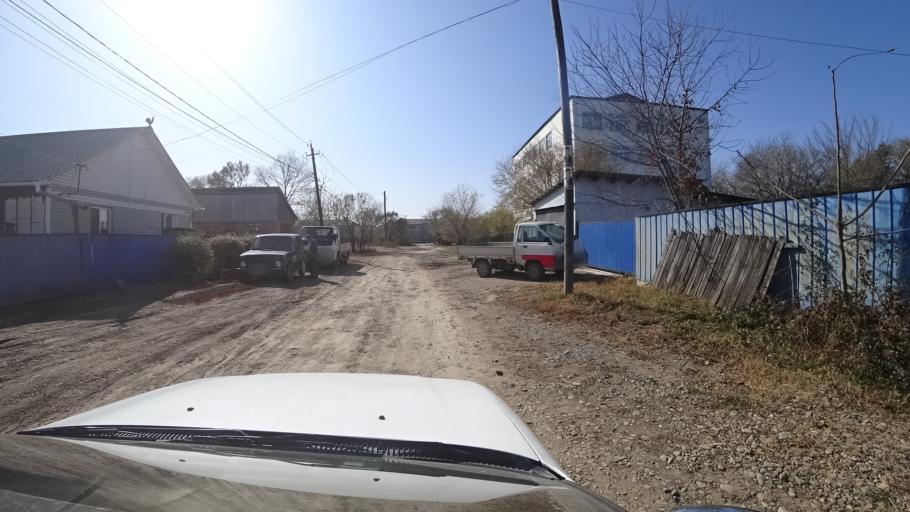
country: RU
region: Primorskiy
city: Dal'nerechensk
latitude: 45.9319
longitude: 133.7506
